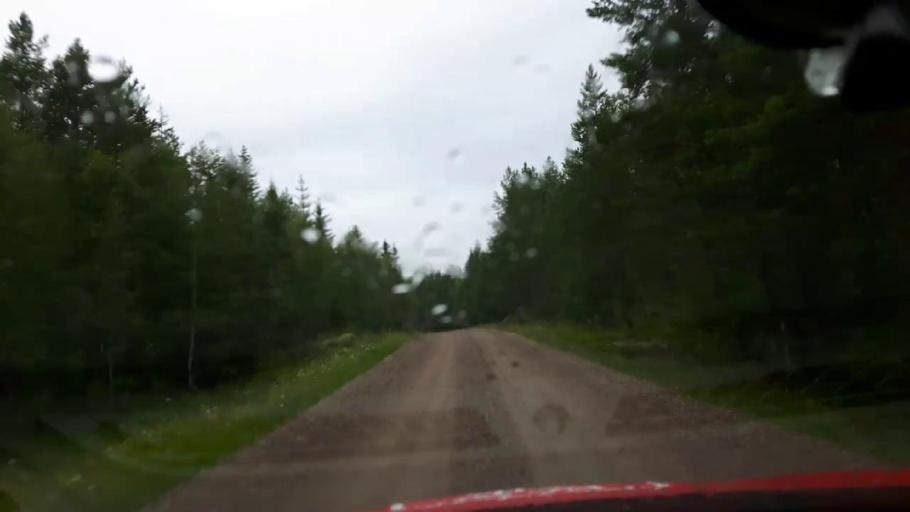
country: SE
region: Jaemtland
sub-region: OEstersunds Kommun
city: Brunflo
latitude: 62.8086
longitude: 14.8935
